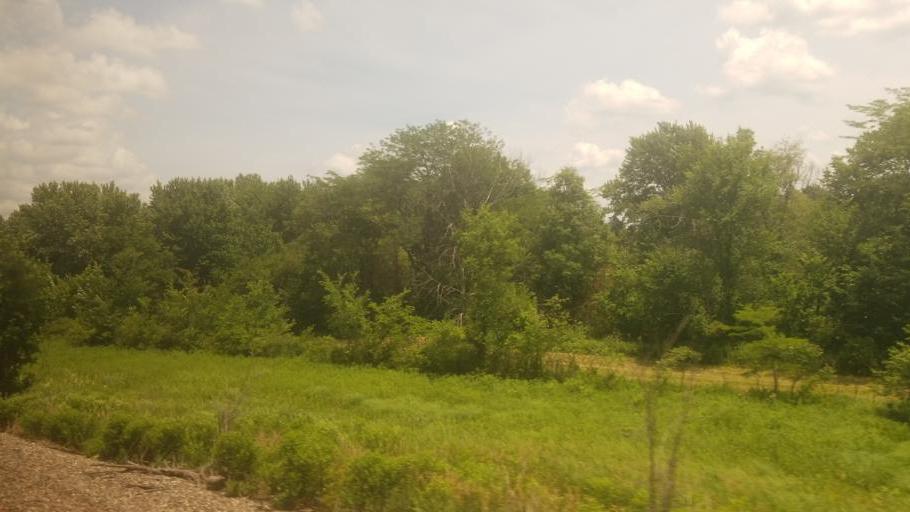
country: US
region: Missouri
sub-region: Macon County
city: La Plata
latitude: 40.0577
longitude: -92.4636
